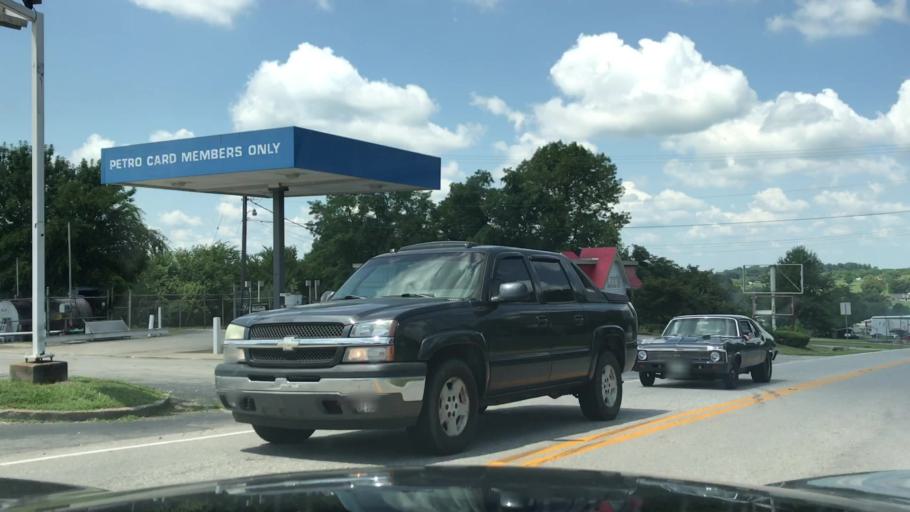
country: US
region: Kentucky
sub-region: Adair County
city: Columbia
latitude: 37.0989
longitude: -85.3143
